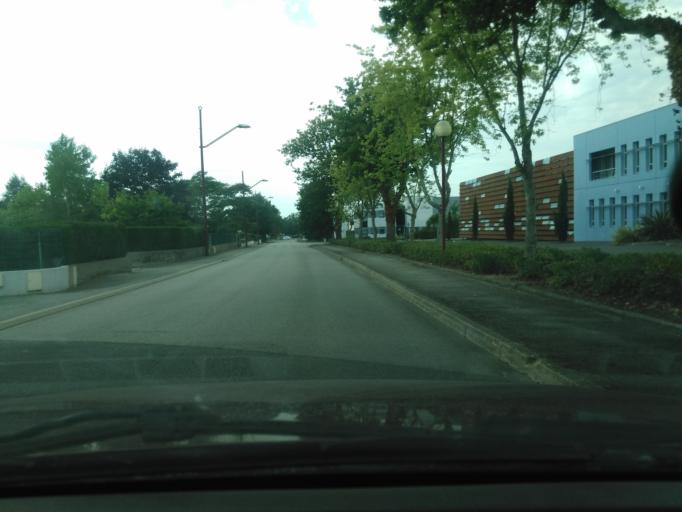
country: FR
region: Pays de la Loire
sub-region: Departement de la Vendee
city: La Ferriere
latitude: 46.7166
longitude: -1.3250
